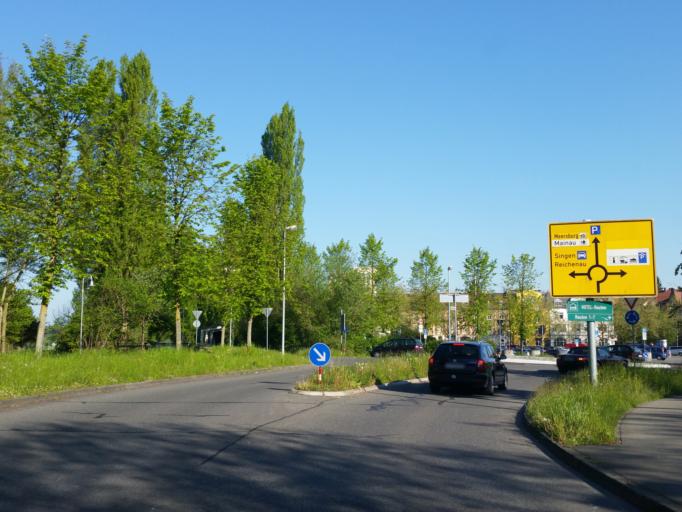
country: DE
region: Baden-Wuerttemberg
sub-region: Freiburg Region
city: Konstanz
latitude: 47.6568
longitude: 9.1692
